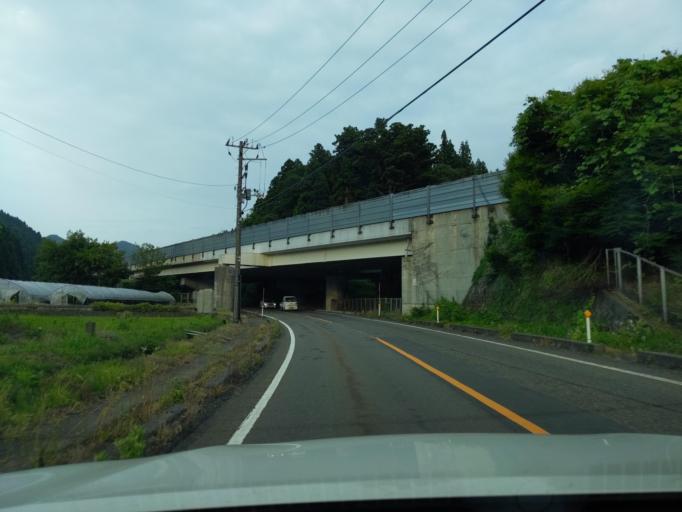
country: JP
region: Niigata
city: Kashiwazaki
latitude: 37.4460
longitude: 138.6686
